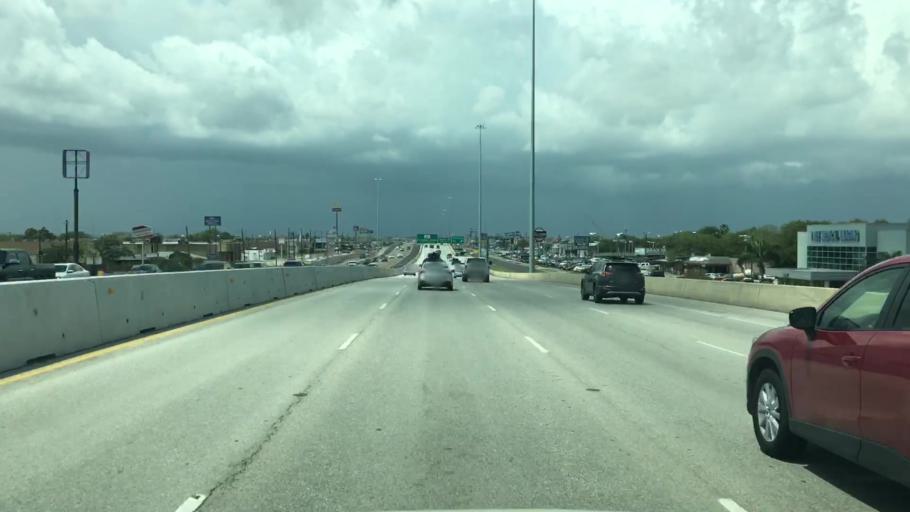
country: US
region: Texas
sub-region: Nueces County
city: Corpus Christi
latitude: 27.7255
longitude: -97.4065
